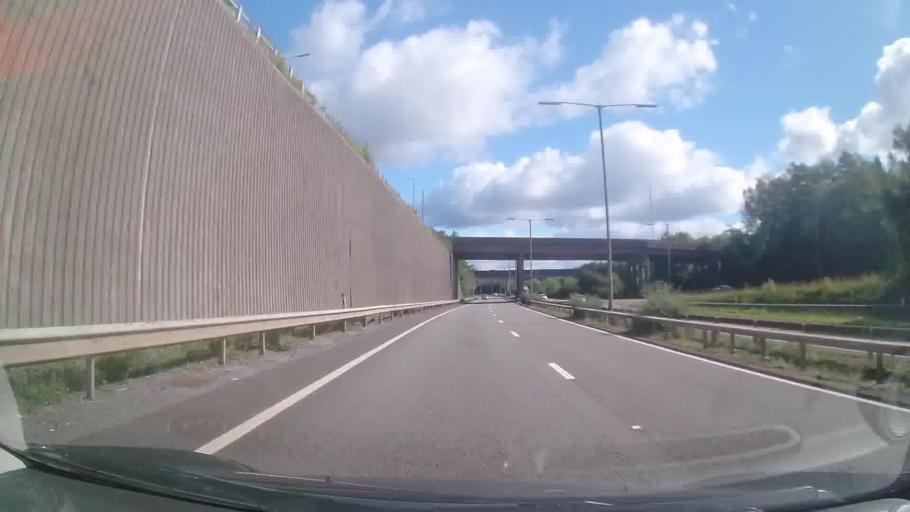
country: GB
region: Wales
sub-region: Neath Port Talbot
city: Neath
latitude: 51.6772
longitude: -3.7832
